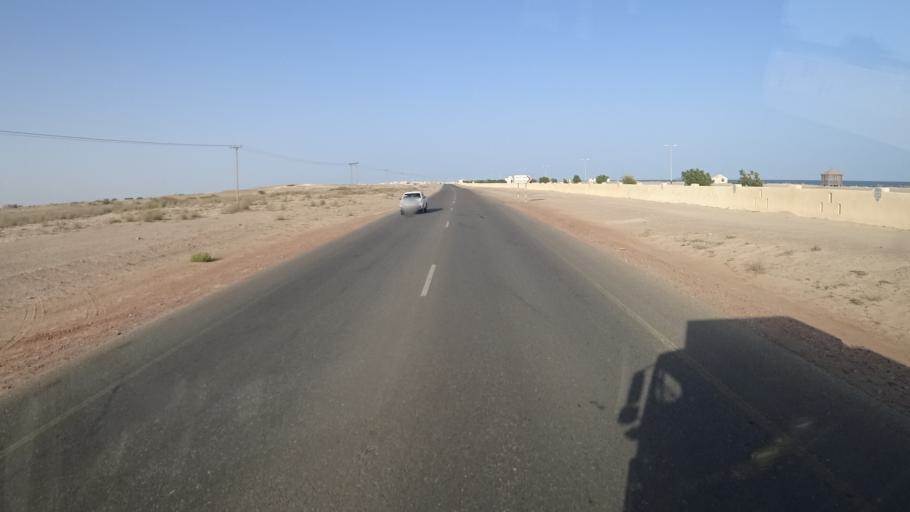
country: OM
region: Ash Sharqiyah
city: Sur
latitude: 22.1576
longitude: 59.7447
